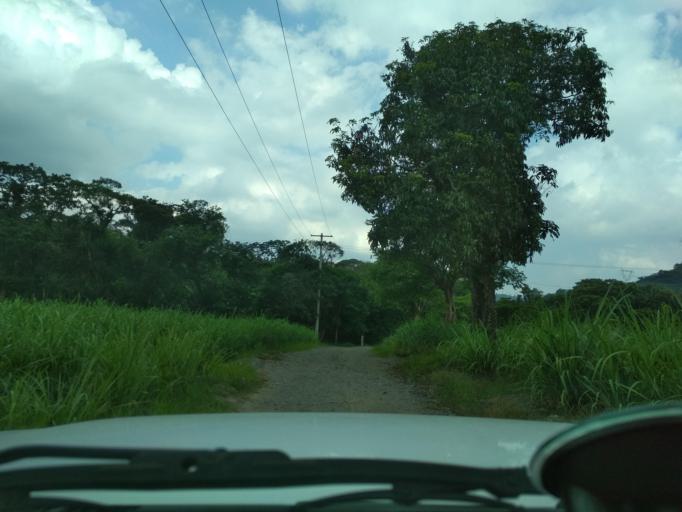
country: MX
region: Veracruz
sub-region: Ixtaczoquitlan
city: Buenavista
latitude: 18.9017
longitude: -97.0269
